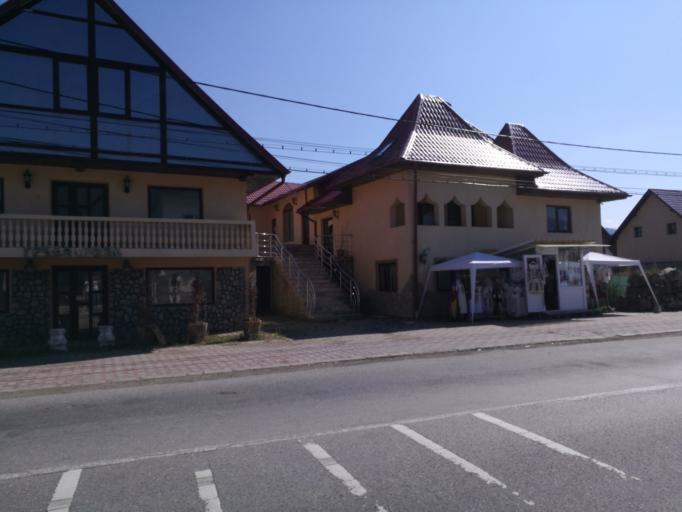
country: RO
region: Suceava
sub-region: Comuna Marginea
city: Marginea
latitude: 47.8011
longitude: 25.7948
